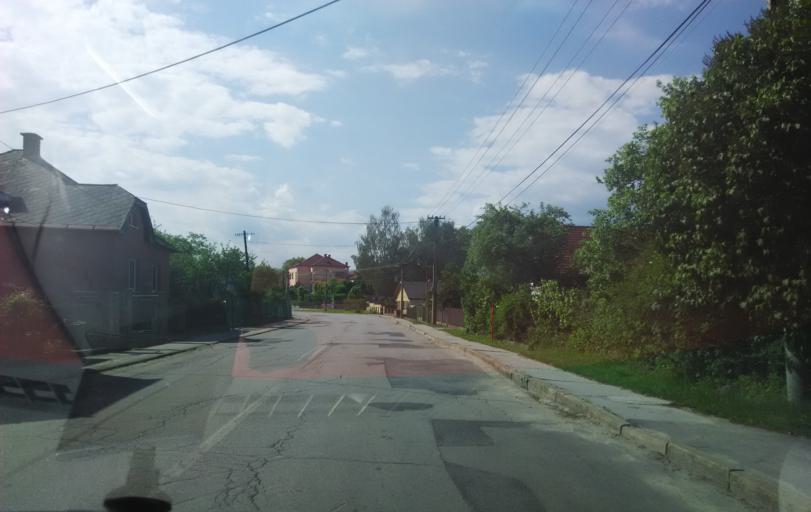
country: SK
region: Banskobystricky
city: Revuca
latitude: 48.6571
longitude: 20.1911
